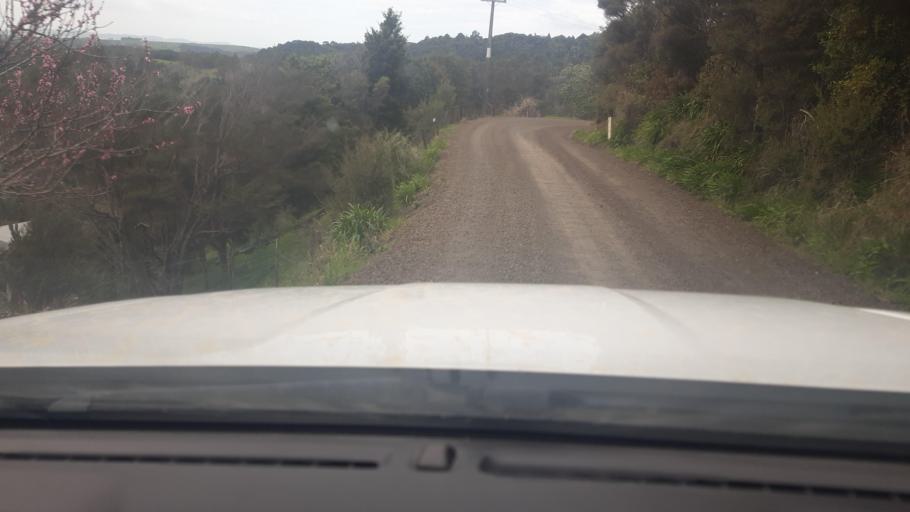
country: NZ
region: Northland
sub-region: Far North District
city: Kaitaia
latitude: -35.0723
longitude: 173.3268
